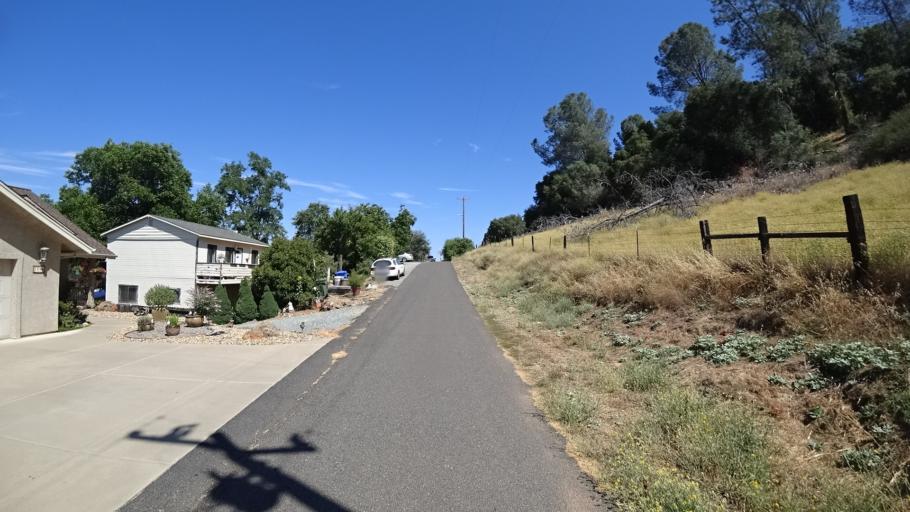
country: US
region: California
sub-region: Calaveras County
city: Angels Camp
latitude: 38.0638
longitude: -120.5365
